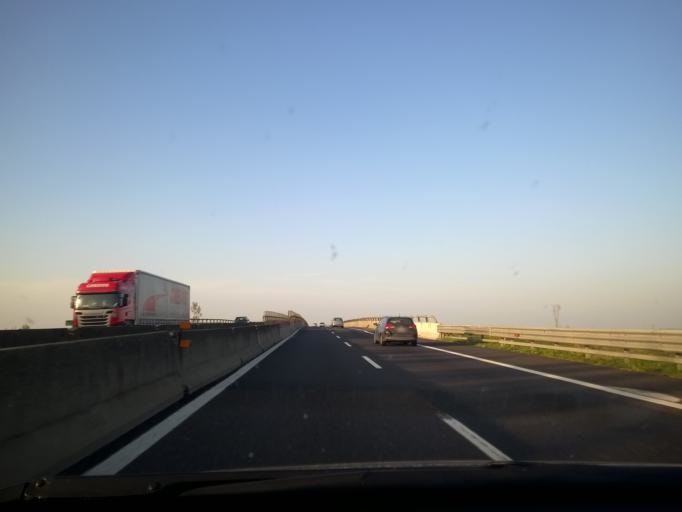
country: IT
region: Emilia-Romagna
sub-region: Provincia di Bologna
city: Malalbergo
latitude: 44.7329
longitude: 11.5161
